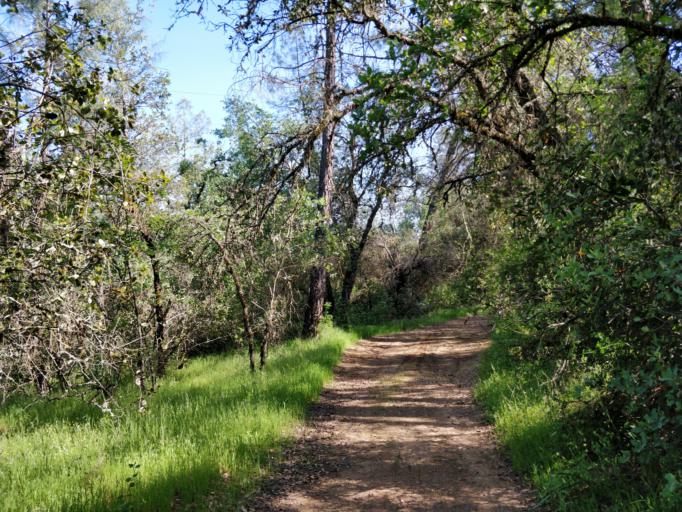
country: US
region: California
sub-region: Shasta County
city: Shasta Lake
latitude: 40.6690
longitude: -122.3638
